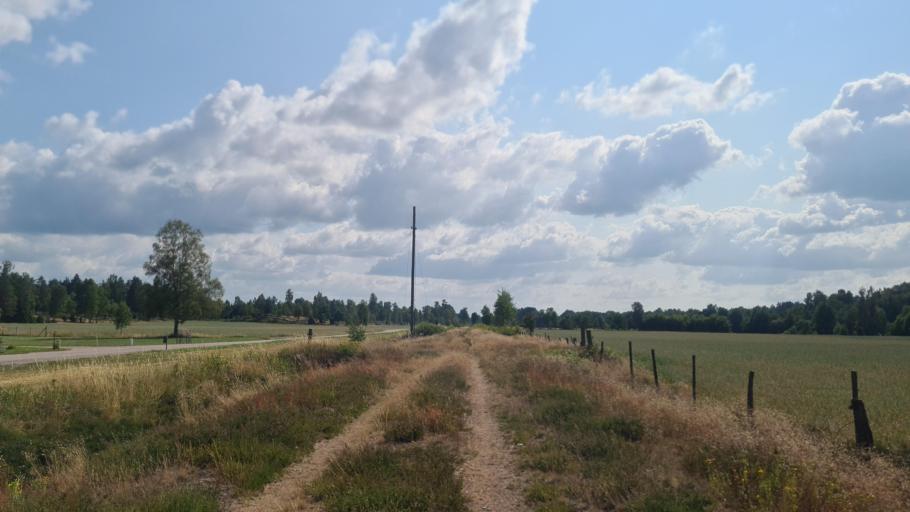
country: SE
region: Kronoberg
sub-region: Ljungby Kommun
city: Ljungby
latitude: 56.7531
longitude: 13.8846
